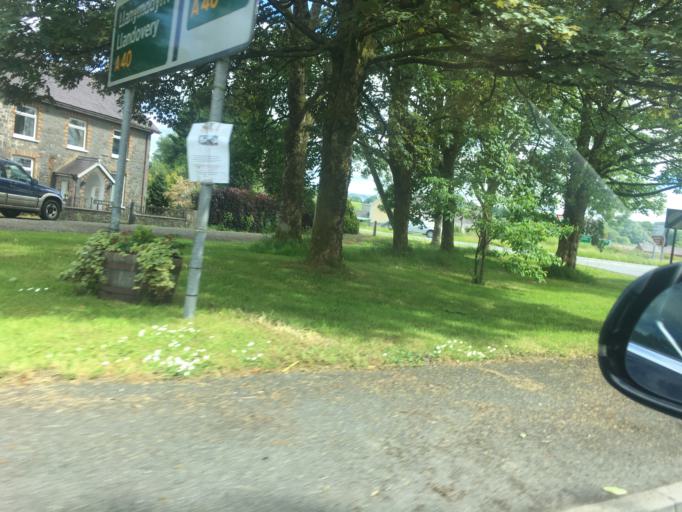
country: GB
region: Wales
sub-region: Carmarthenshire
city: Llansadwrn
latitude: 51.9675
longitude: -3.8735
